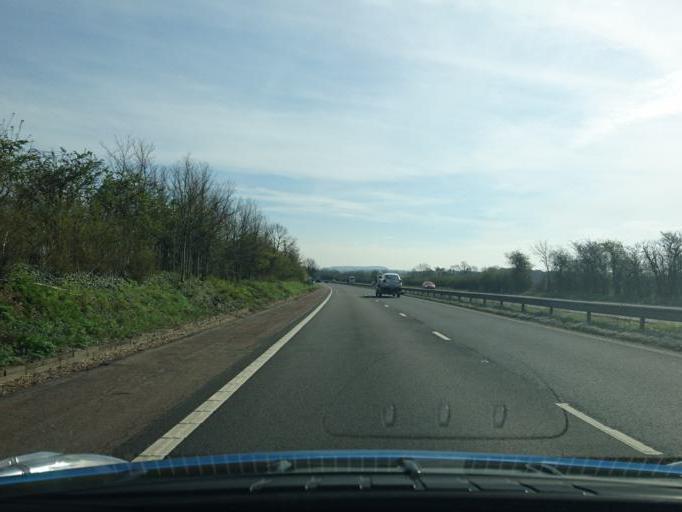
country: GB
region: England
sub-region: Worcestershire
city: Upton upon Severn
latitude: 51.9974
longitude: -2.2954
